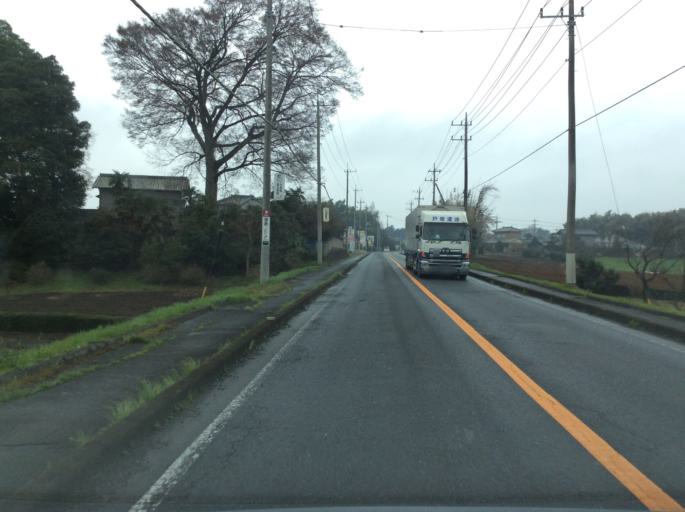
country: JP
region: Ibaraki
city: Mitsukaido
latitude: 35.9862
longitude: 139.9417
